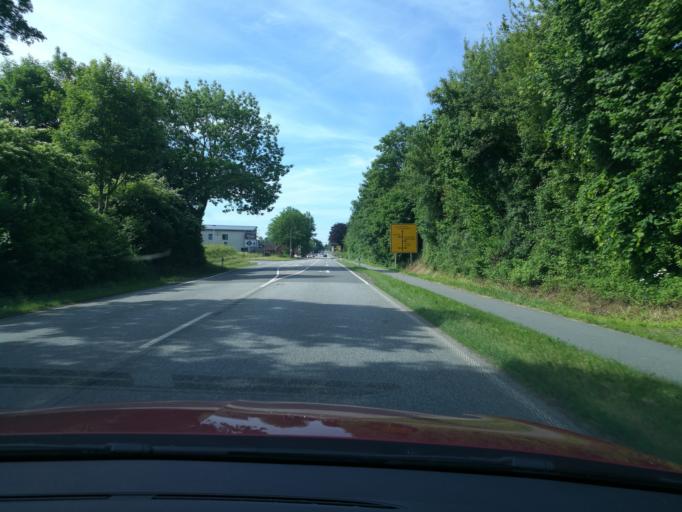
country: DE
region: Schleswig-Holstein
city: Elmenhorst
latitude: 53.7690
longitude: 10.2667
